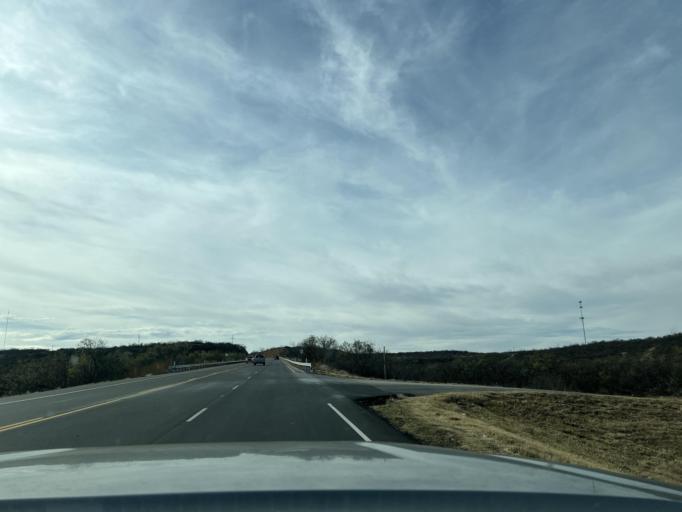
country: US
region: Texas
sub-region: Shackelford County
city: Albany
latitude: 32.7180
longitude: -99.3098
